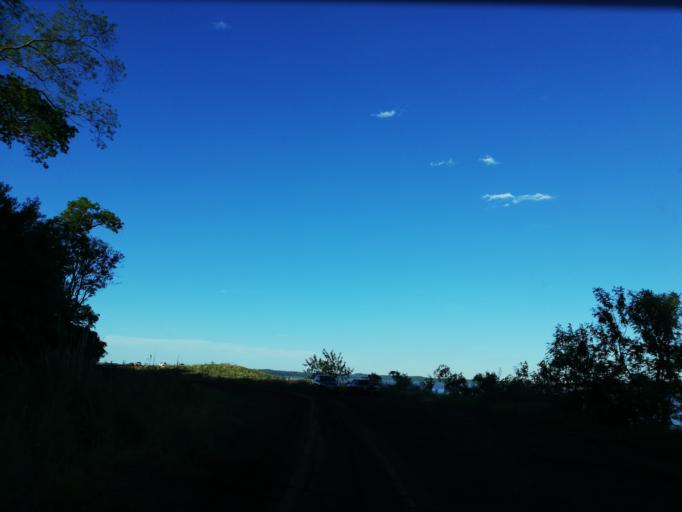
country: AR
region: Misiones
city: Garupa
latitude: -27.4598
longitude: -55.8136
